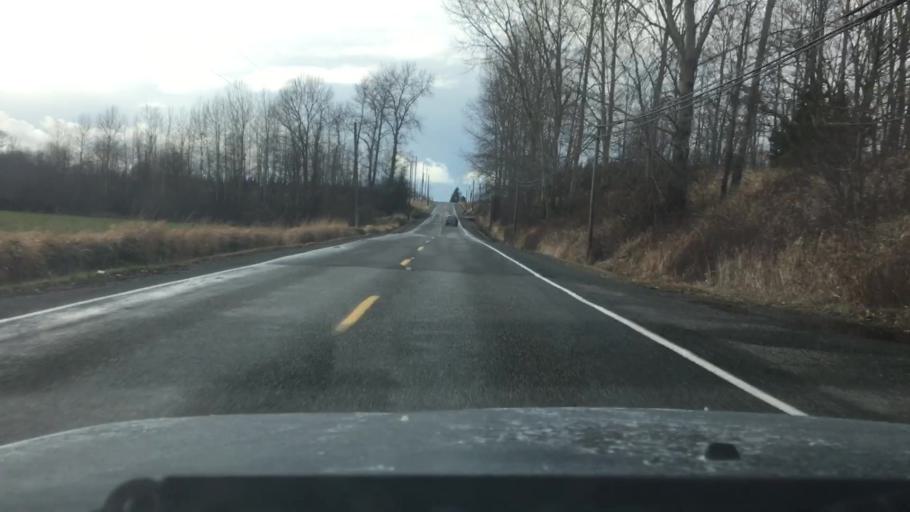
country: US
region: Washington
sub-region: Whatcom County
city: Ferndale
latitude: 48.8484
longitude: -122.6773
